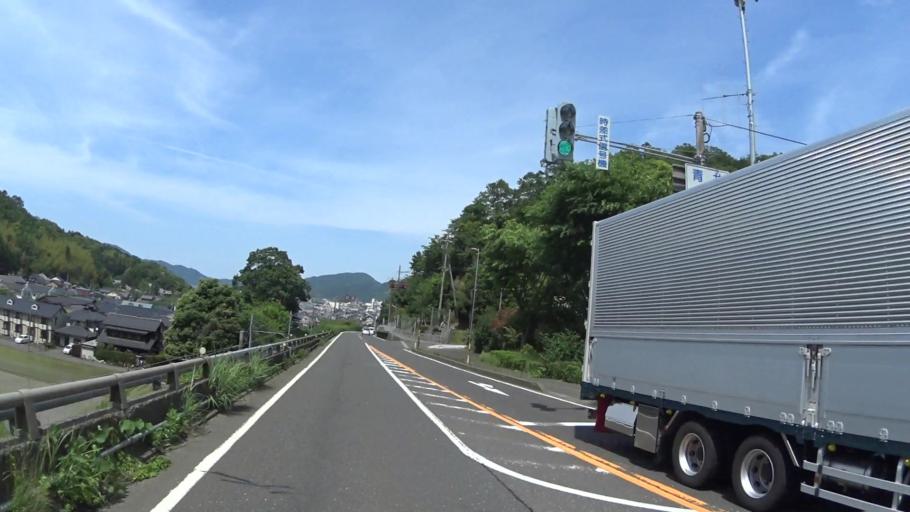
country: JP
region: Fukui
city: Obama
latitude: 35.4862
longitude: 135.7303
